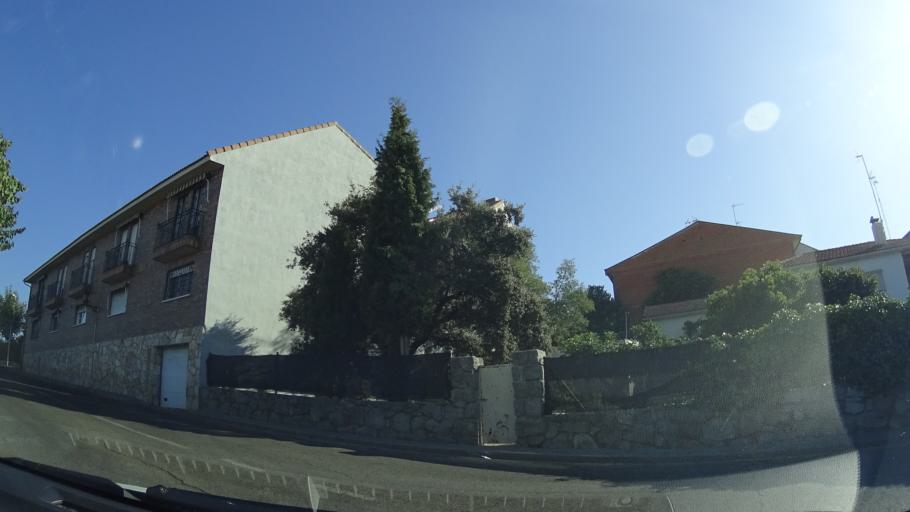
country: ES
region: Madrid
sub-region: Provincia de Madrid
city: Colmenarejo
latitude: 40.5581
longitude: -4.0175
